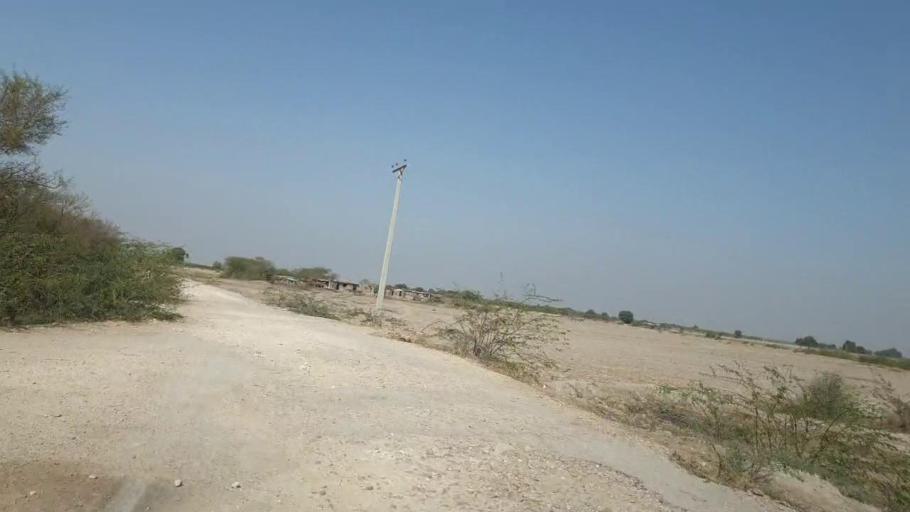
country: PK
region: Sindh
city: Nabisar
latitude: 24.9973
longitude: 69.5291
